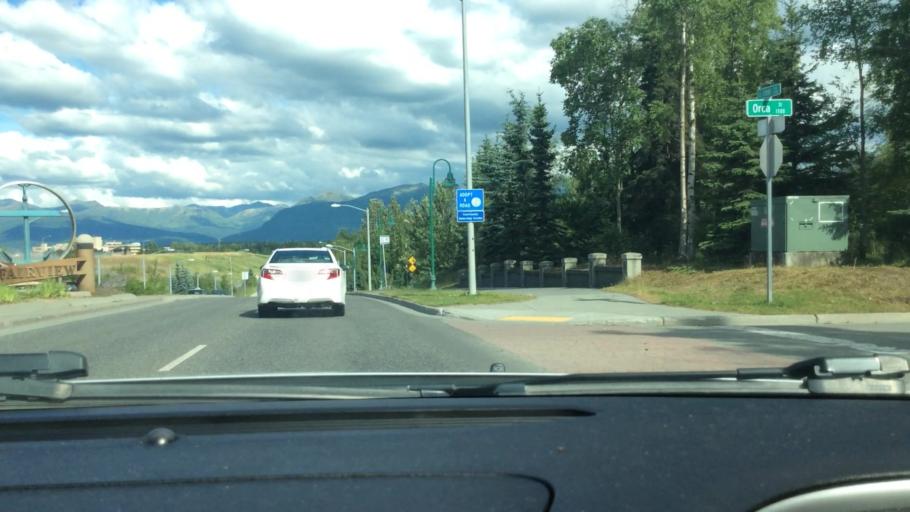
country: US
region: Alaska
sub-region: Anchorage Municipality
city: Anchorage
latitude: 61.2076
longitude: -149.8549
